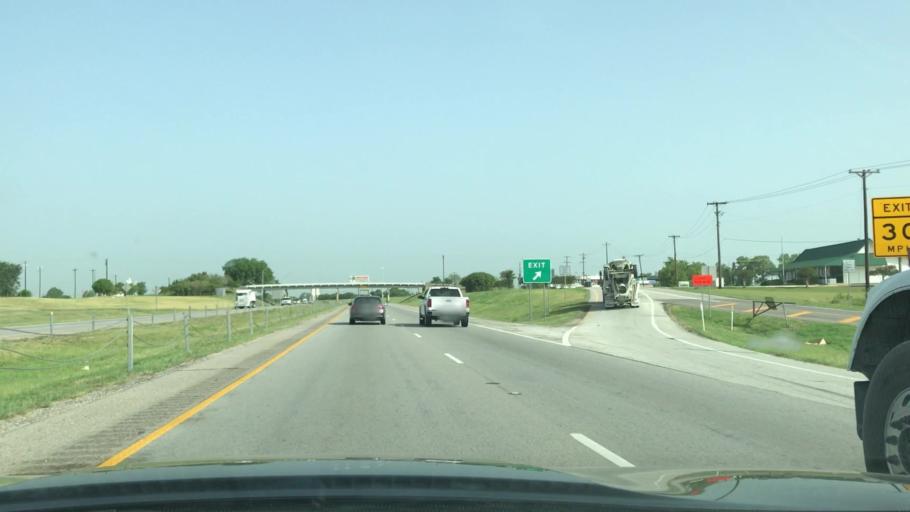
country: US
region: Texas
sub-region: Kaufman County
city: Forney
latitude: 32.7680
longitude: -96.4885
